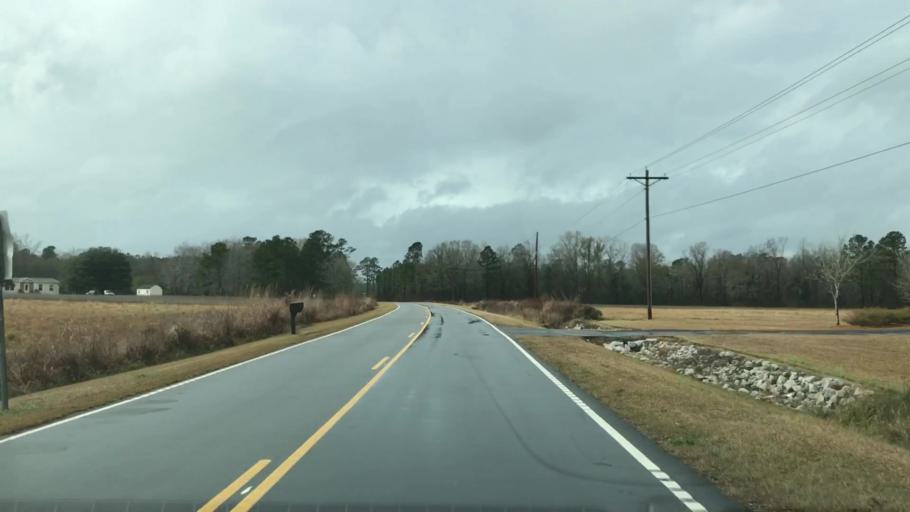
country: US
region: South Carolina
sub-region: Florence County
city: Johnsonville
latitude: 33.6751
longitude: -79.3318
